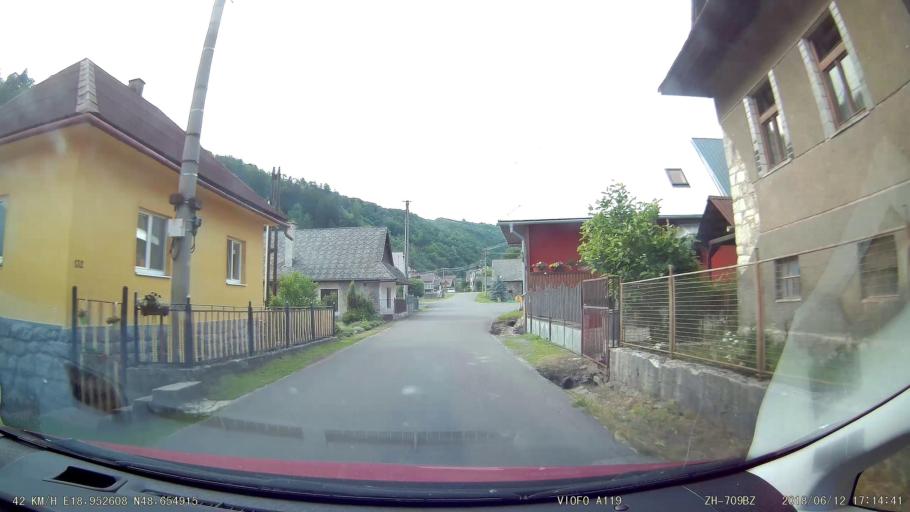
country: SK
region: Banskobystricky
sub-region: Okres Ziar nad Hronom
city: Kremnica
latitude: 48.6551
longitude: 18.9525
